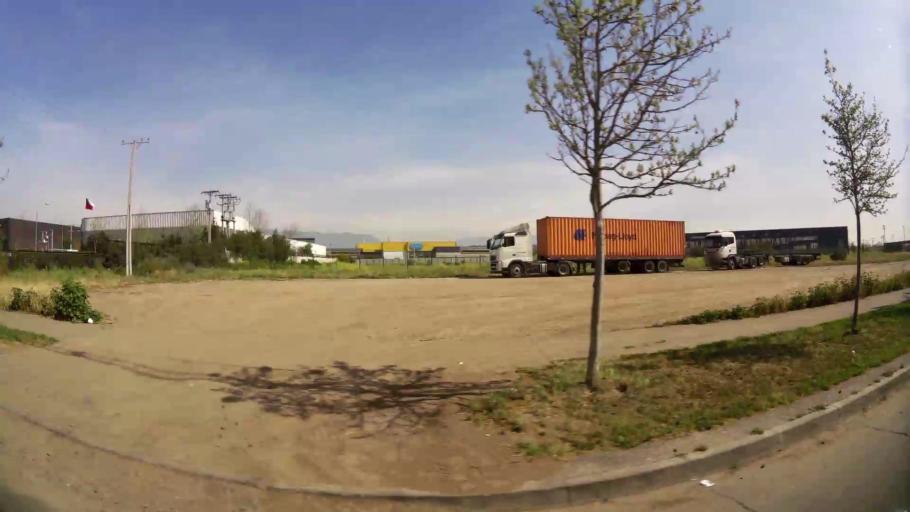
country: CL
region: Santiago Metropolitan
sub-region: Provincia de Santiago
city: Lo Prado
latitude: -33.4259
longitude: -70.7771
